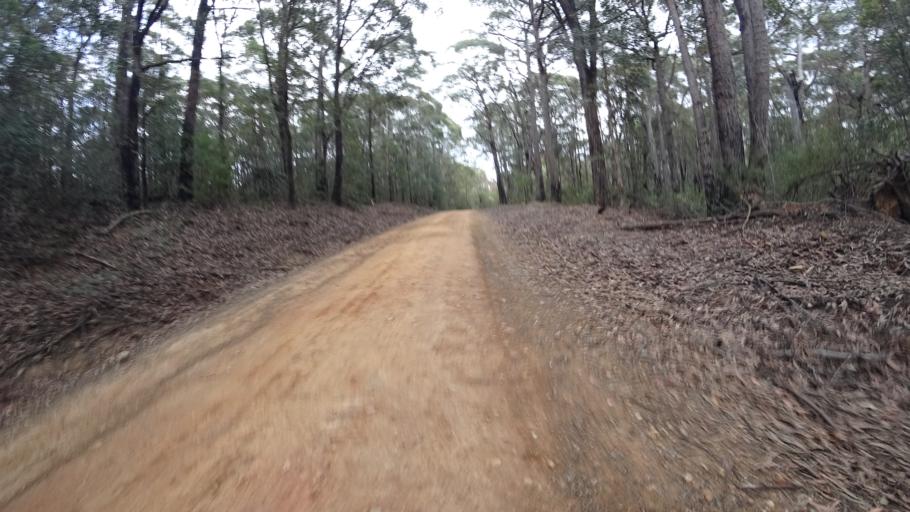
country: AU
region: New South Wales
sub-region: Shoalhaven Shire
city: Milton
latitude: -35.1669
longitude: 150.4098
